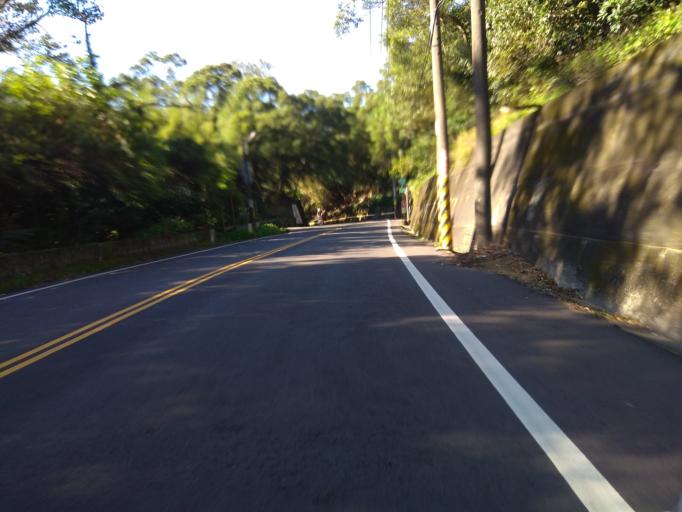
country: TW
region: Taiwan
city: Daxi
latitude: 24.8613
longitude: 121.1547
